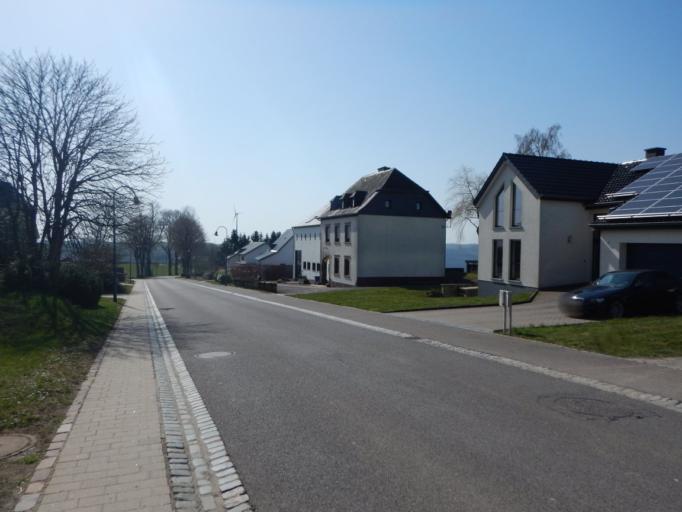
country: LU
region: Diekirch
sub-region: Canton de Diekirch
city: Bourscheid
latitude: 49.9435
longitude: 6.0830
